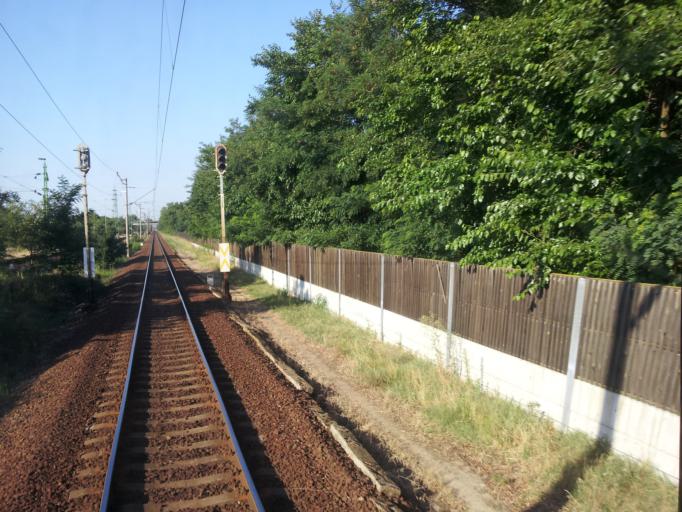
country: HU
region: Pest
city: Dunaharaszti
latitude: 47.3721
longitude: 19.1116
